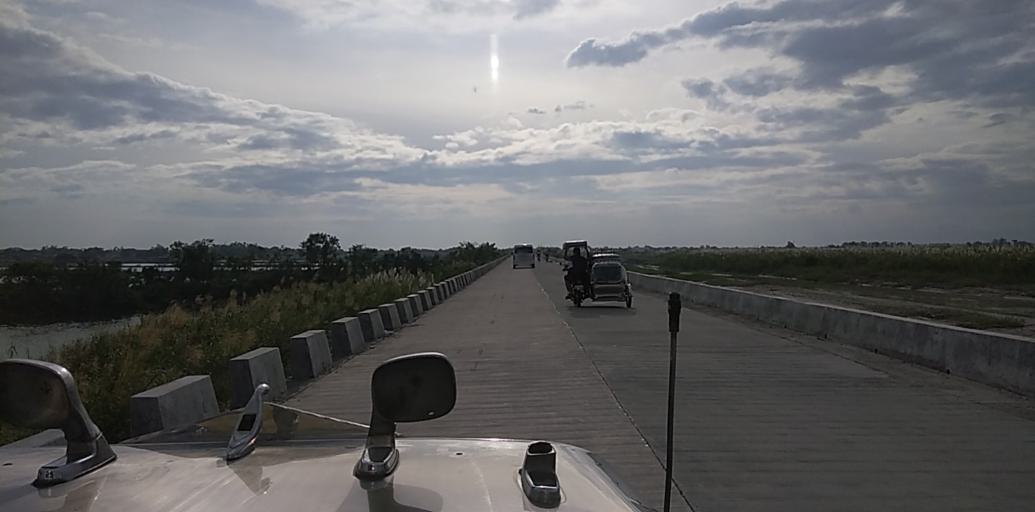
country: PH
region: Central Luzon
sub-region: Province of Pampanga
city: Minalin
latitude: 14.9694
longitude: 120.6758
